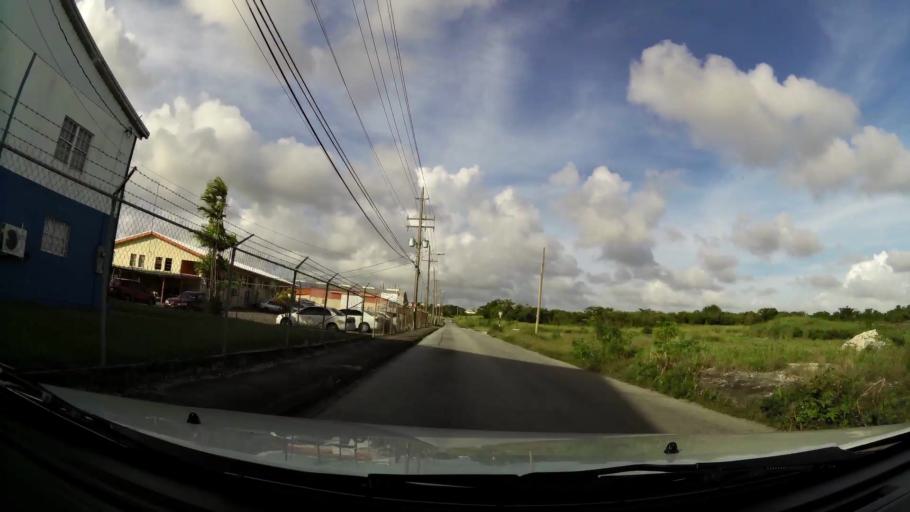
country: BB
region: Christ Church
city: Oistins
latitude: 13.0804
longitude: -59.5572
